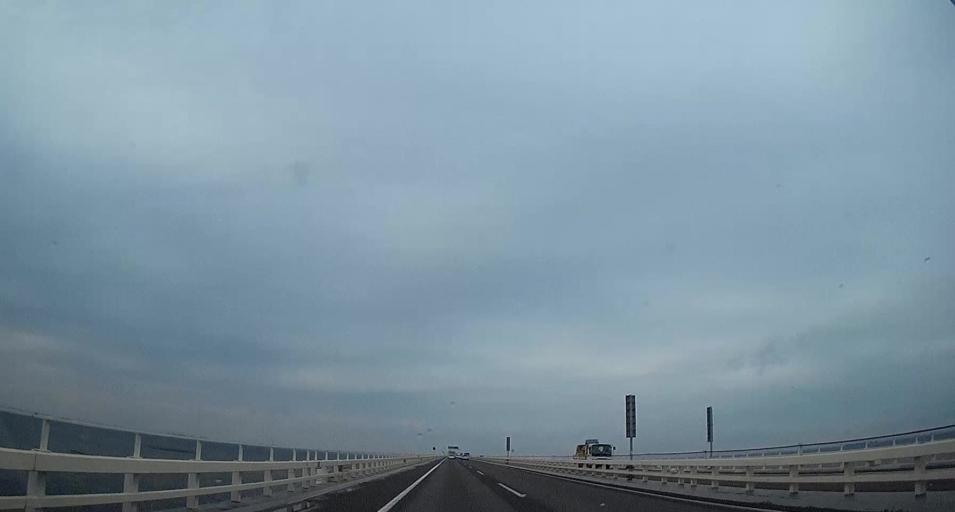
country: JP
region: Chiba
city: Kisarazu
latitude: 35.4412
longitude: 139.9083
